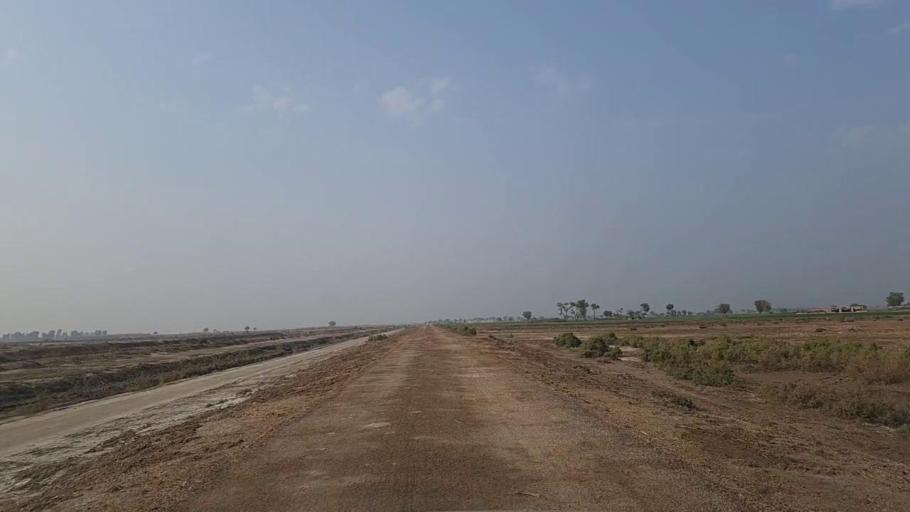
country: PK
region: Sindh
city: Nawabshah
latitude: 26.3275
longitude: 68.4784
